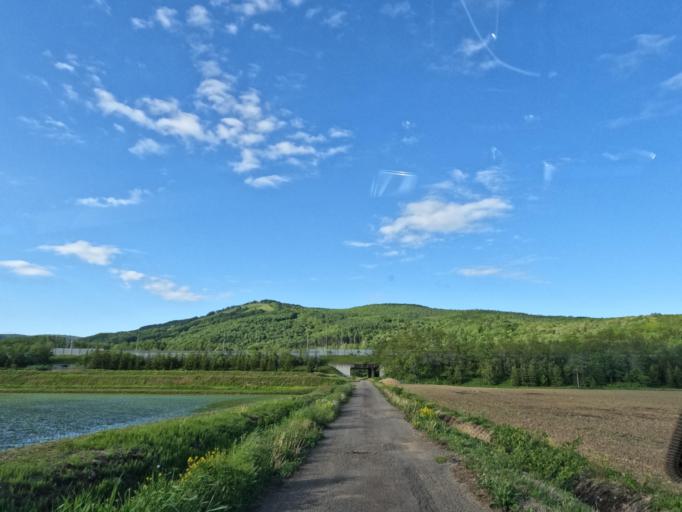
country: JP
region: Hokkaido
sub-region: Asahikawa-shi
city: Asahikawa
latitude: 43.9199
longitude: 142.4939
